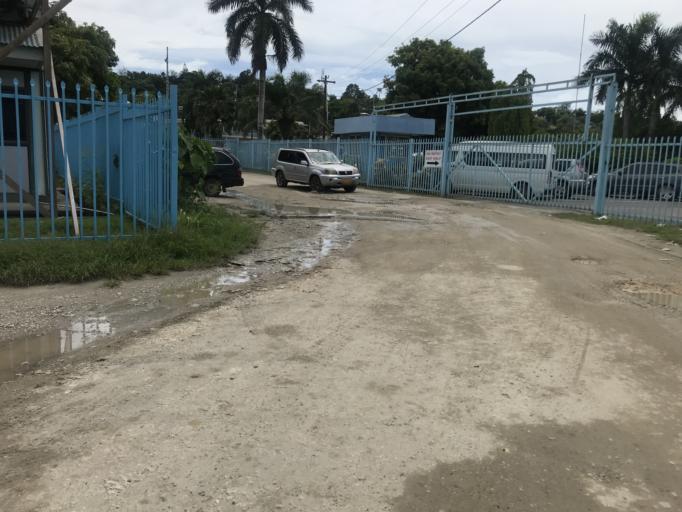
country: SB
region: Guadalcanal
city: Honiara
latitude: -9.4299
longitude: 159.9516
